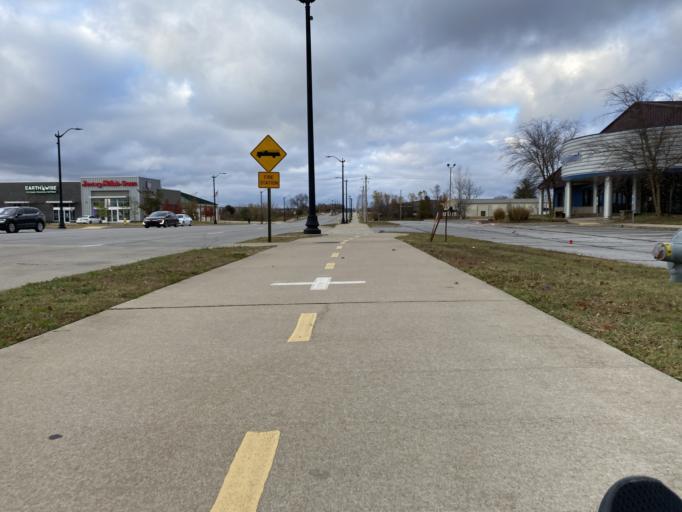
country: US
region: Arkansas
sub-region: Benton County
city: Bentonville
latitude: 36.3366
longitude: -94.2223
